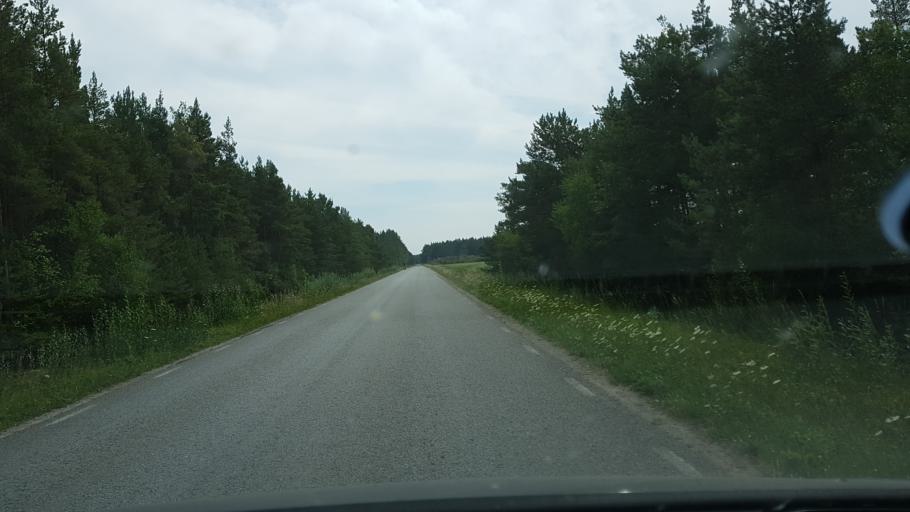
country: SE
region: Gotland
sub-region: Gotland
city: Visby
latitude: 57.7287
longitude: 18.5064
